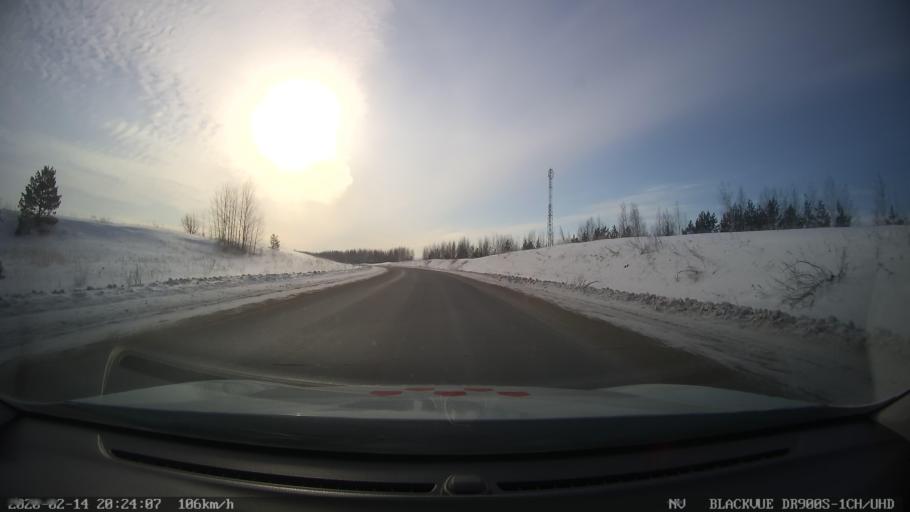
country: RU
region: Tatarstan
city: Verkhniy Uslon
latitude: 55.5174
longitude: 48.9671
